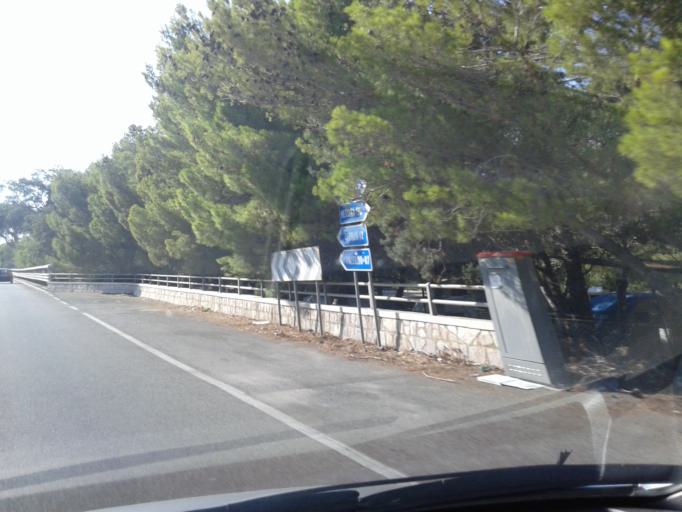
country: IT
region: Sicily
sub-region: Palermo
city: Finale
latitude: 38.0230
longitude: 14.1535
